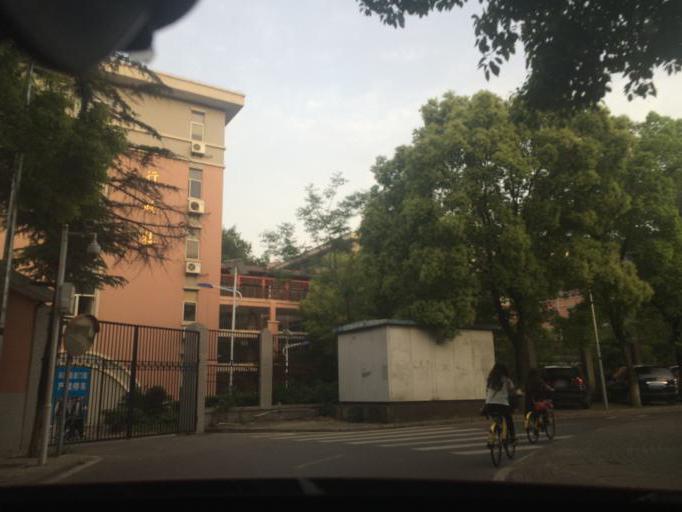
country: CN
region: Hubei
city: Guanshan
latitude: 30.5319
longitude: 114.3574
